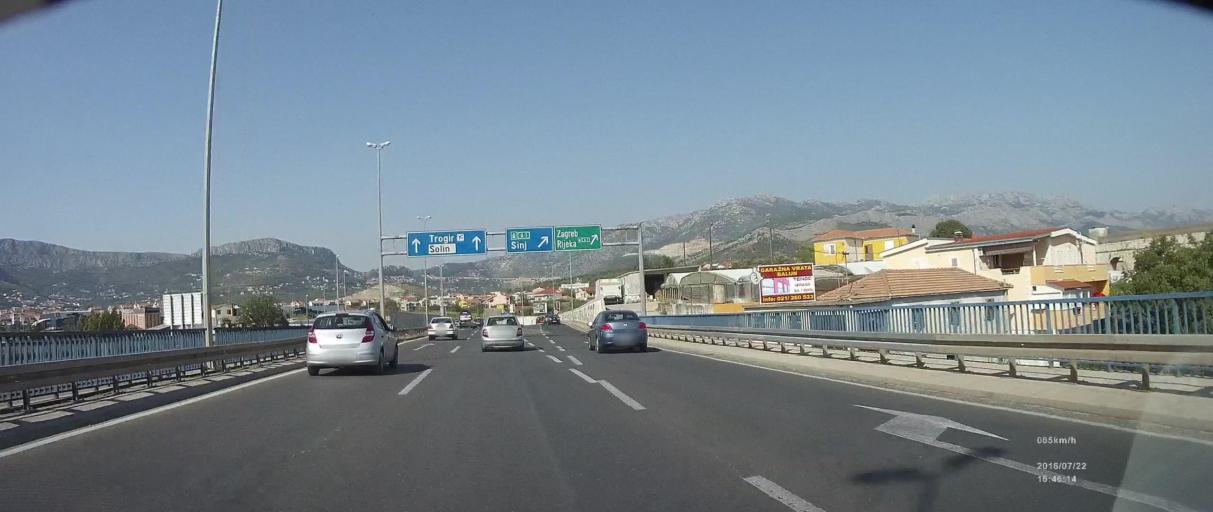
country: HR
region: Splitsko-Dalmatinska
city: Solin
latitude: 43.5247
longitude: 16.4886
